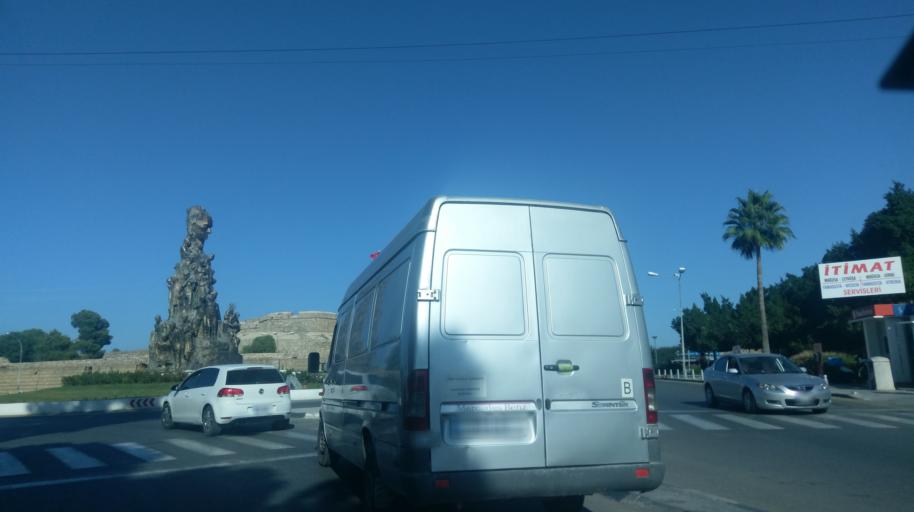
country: CY
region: Ammochostos
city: Famagusta
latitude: 35.1200
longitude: 33.9382
